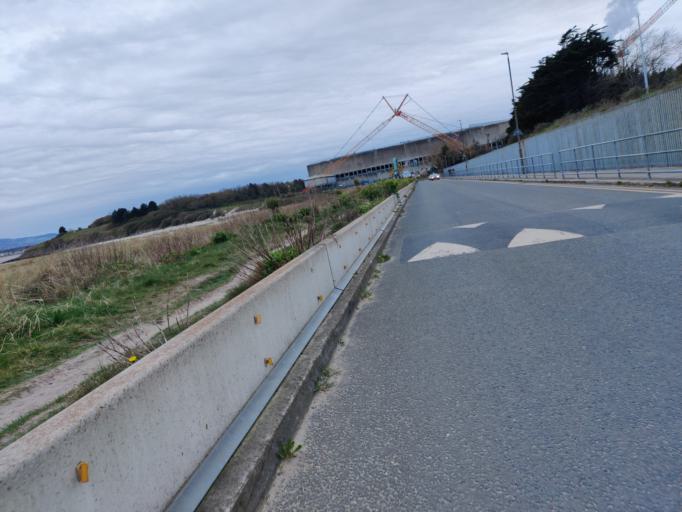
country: IE
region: Leinster
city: Sandymount
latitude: 53.3376
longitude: -6.1901
